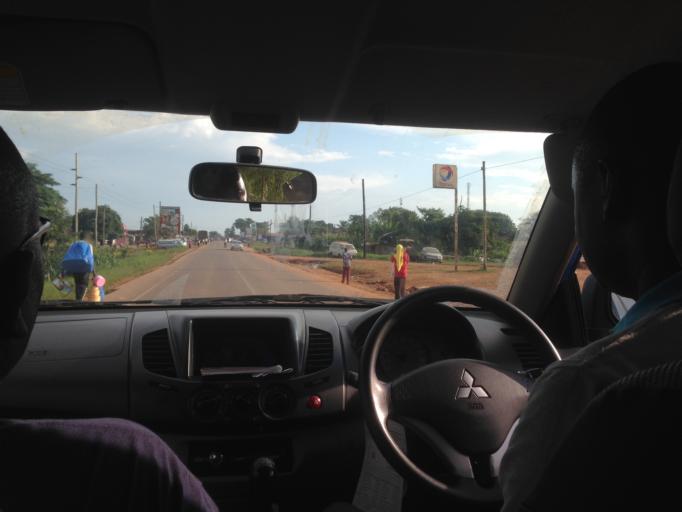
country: UG
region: Western Region
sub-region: Kiryandongo District
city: Kiryandongo
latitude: 1.8118
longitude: 32.0128
